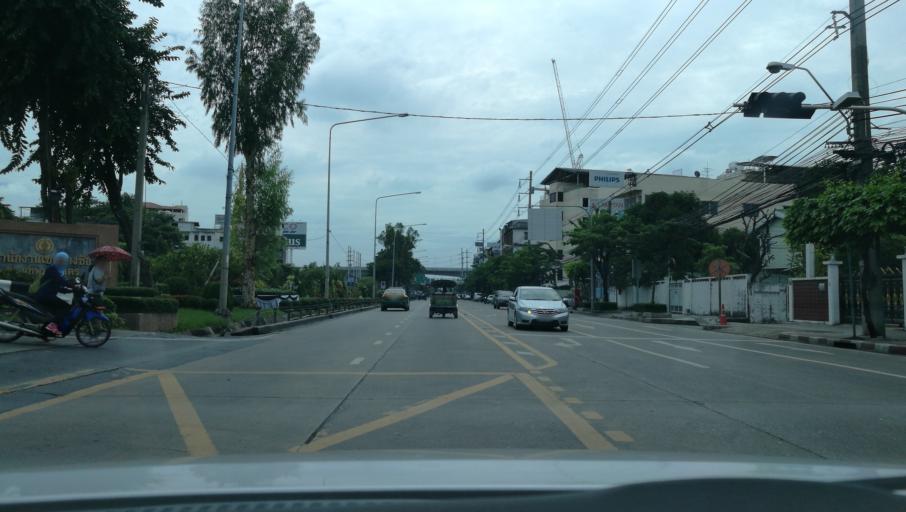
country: TH
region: Bangkok
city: Bang Sue
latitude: 13.8093
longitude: 100.5341
